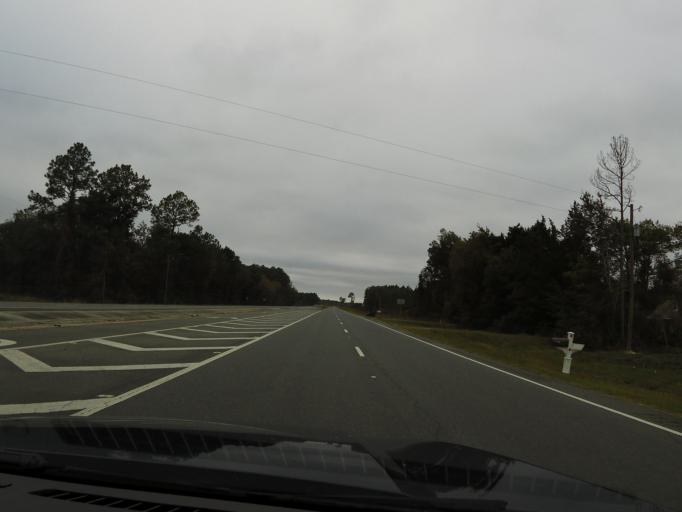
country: US
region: Georgia
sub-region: Charlton County
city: Folkston
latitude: 30.9108
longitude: -82.0757
